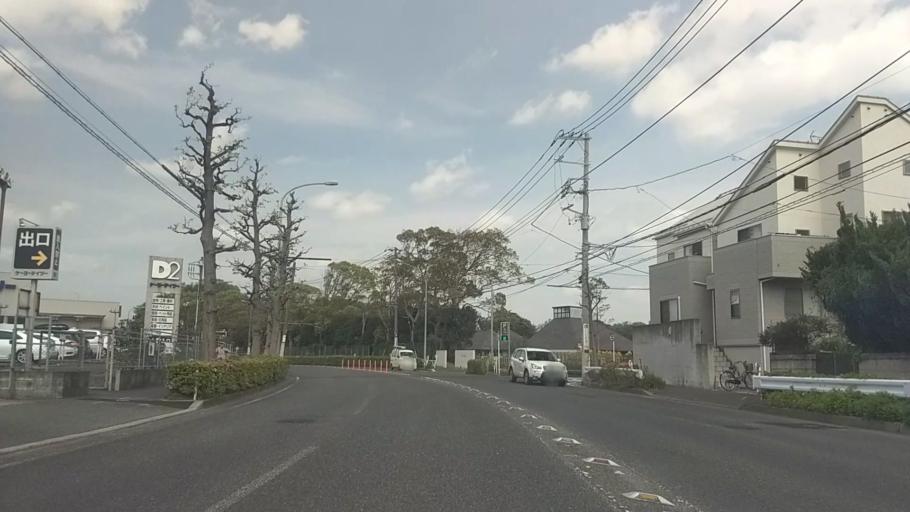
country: JP
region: Kanagawa
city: Yokohama
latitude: 35.3853
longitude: 139.5914
